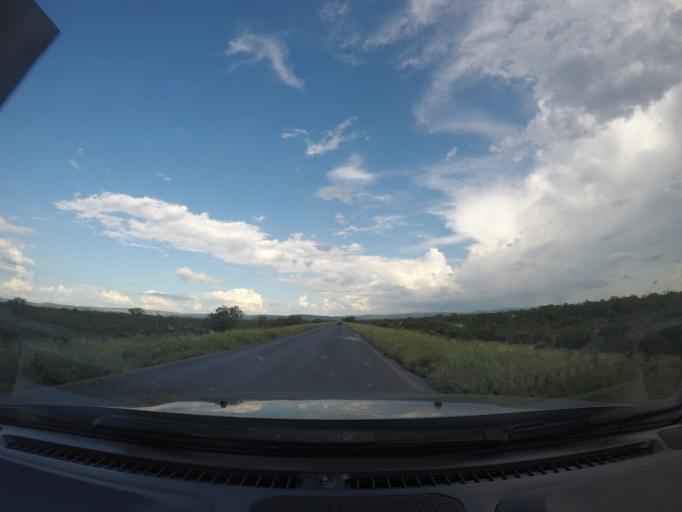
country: BR
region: Bahia
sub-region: Ibotirama
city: Ibotirama
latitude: -12.1669
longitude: -43.2745
